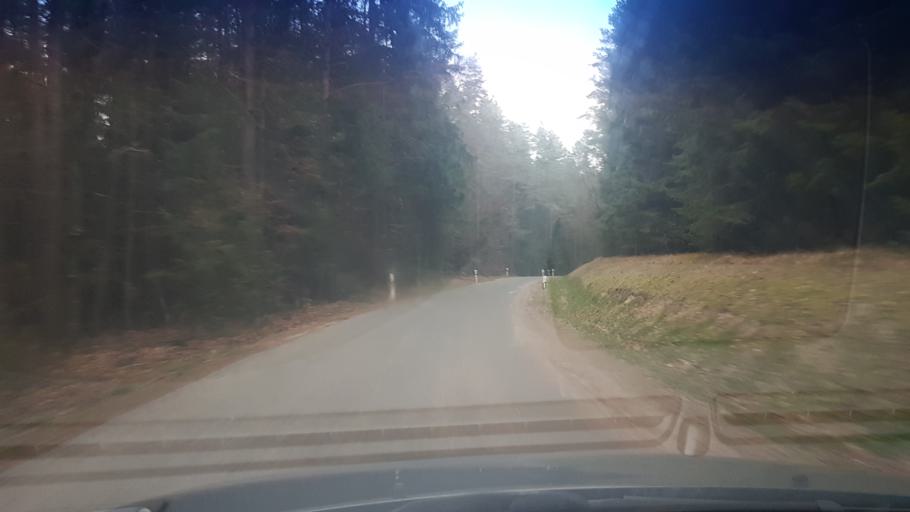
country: DE
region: Bavaria
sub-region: Upper Franconia
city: Weismain
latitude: 50.0477
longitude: 11.2854
